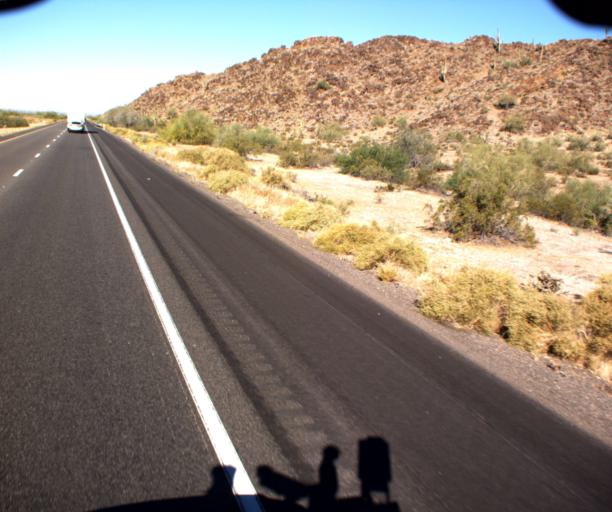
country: US
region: Arizona
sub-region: Maricopa County
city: Gila Bend
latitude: 32.9064
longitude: -112.5654
